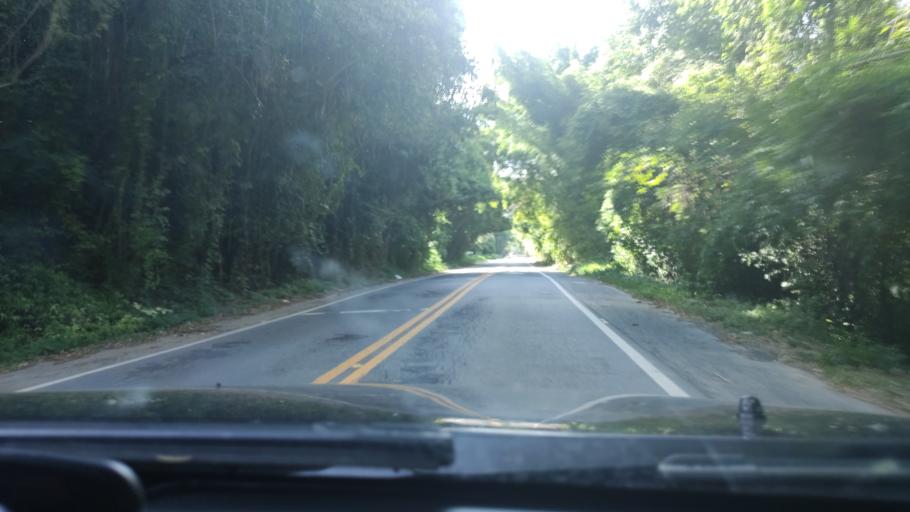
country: BR
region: Sao Paulo
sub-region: Aguas De Lindoia
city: Aguas de Lindoia
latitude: -22.5288
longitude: -46.6392
